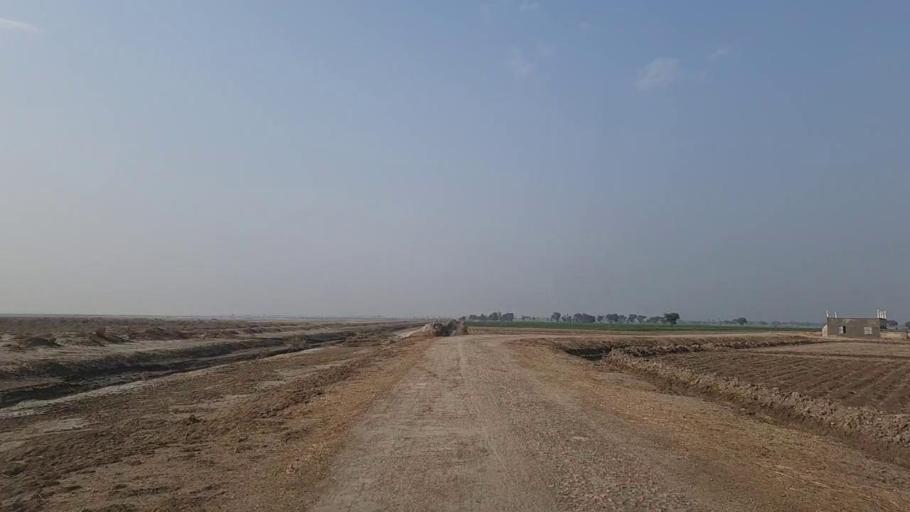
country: PK
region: Sindh
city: Nawabshah
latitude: 26.3338
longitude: 68.4739
